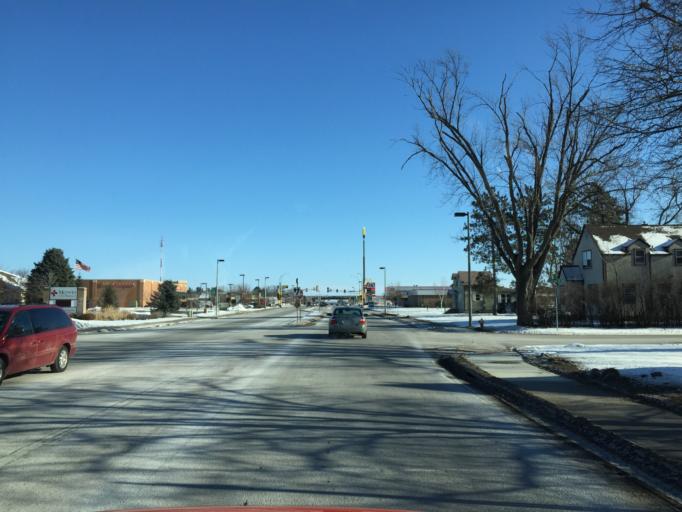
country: US
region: Minnesota
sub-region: Isanti County
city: Cambridge
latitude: 45.5727
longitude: -93.2168
